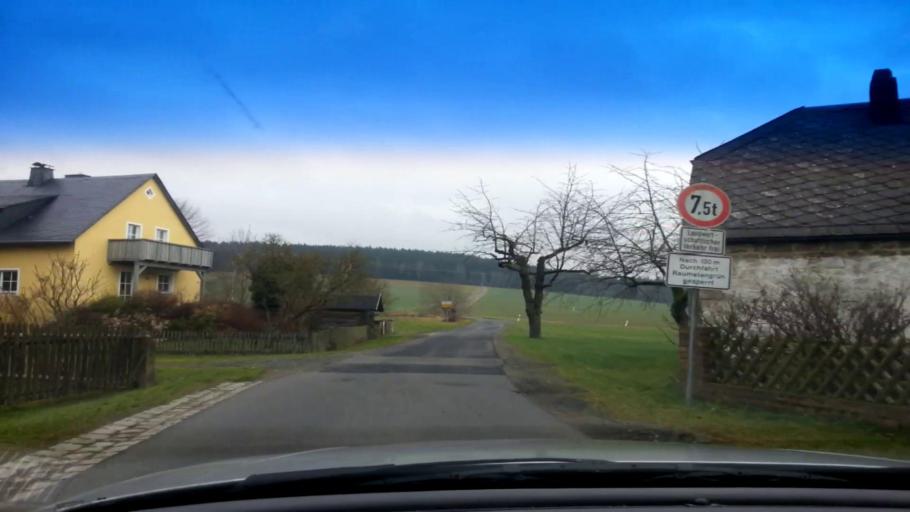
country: DE
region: Bavaria
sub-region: Upper Franconia
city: Kirchenlamitz
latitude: 50.1336
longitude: 11.9375
